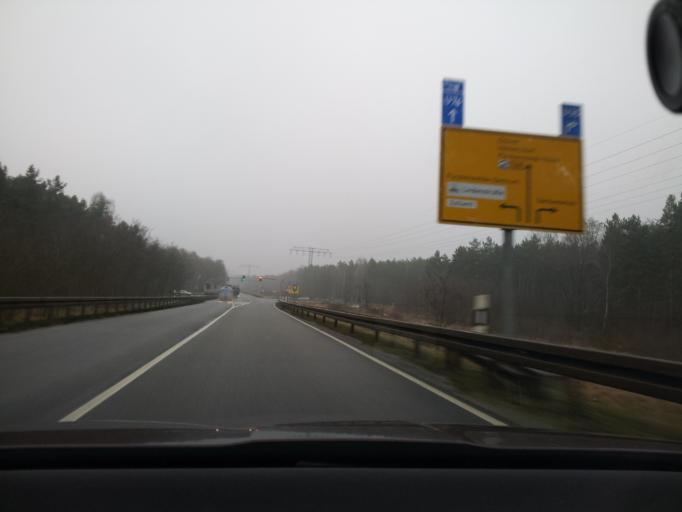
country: DE
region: Brandenburg
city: Langewahl
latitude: 52.3507
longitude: 14.1018
